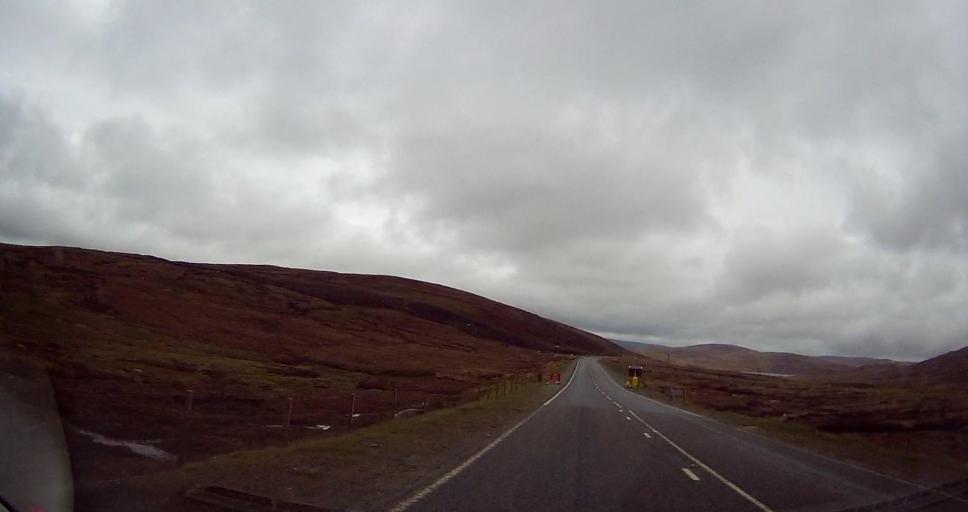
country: GB
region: Scotland
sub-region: Shetland Islands
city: Lerwick
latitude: 60.3268
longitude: -1.2529
